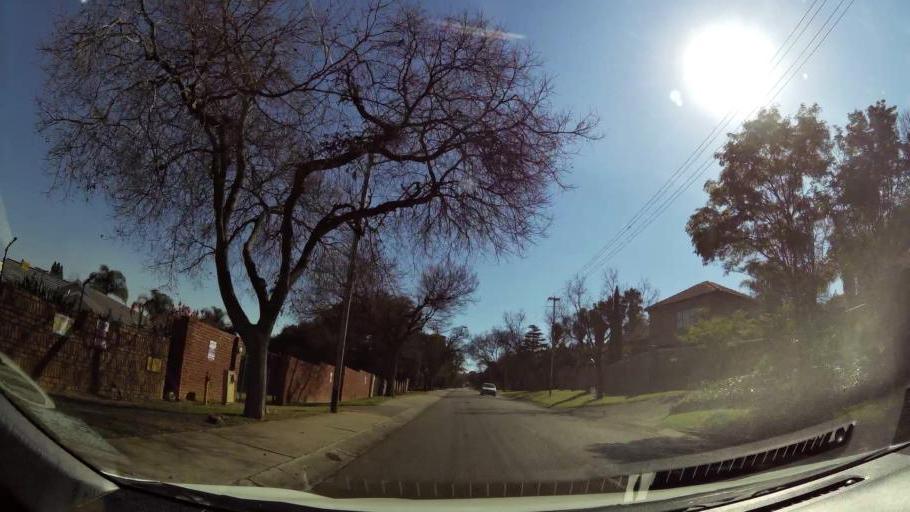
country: ZA
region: Gauteng
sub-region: City of Tshwane Metropolitan Municipality
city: Pretoria
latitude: -25.7965
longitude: 28.2353
